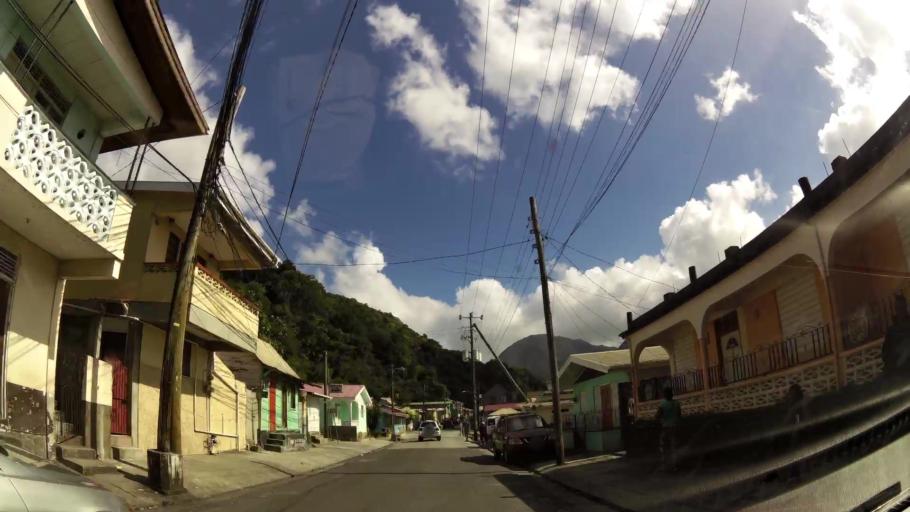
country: DM
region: Saint George
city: Roseau
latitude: 15.2919
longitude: -61.3793
